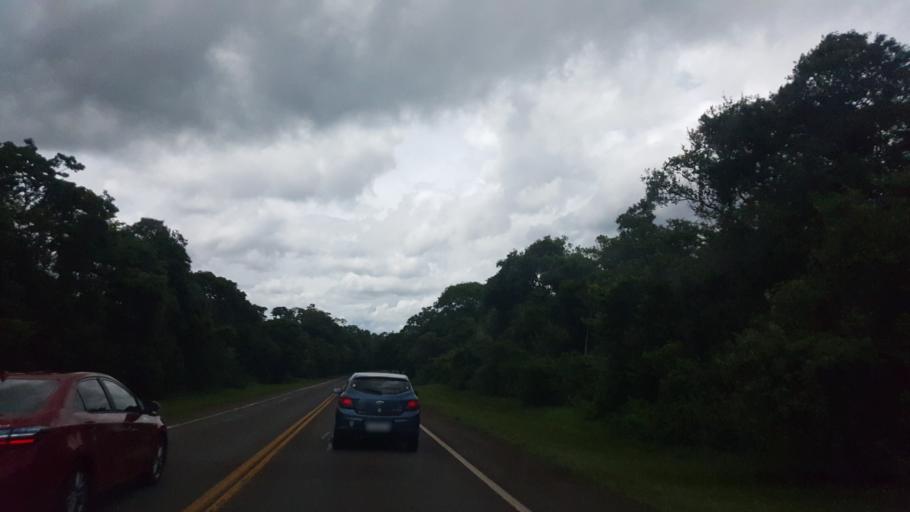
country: AR
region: Misiones
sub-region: Departamento de Iguazu
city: Puerto Iguazu
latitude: -25.6942
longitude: -54.5148
